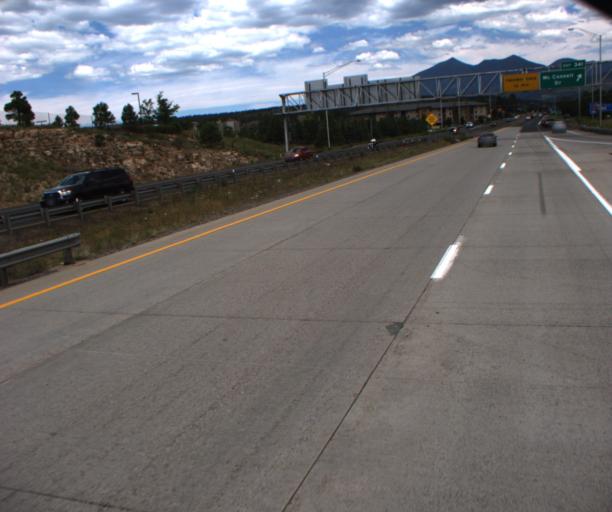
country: US
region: Arizona
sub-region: Coconino County
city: Flagstaff
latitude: 35.1741
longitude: -111.6615
